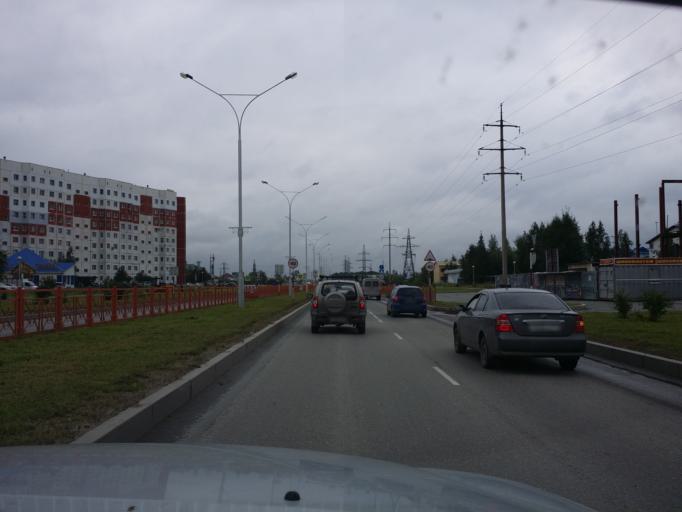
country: RU
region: Khanty-Mansiyskiy Avtonomnyy Okrug
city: Nizhnevartovsk
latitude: 60.9576
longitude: 76.5688
